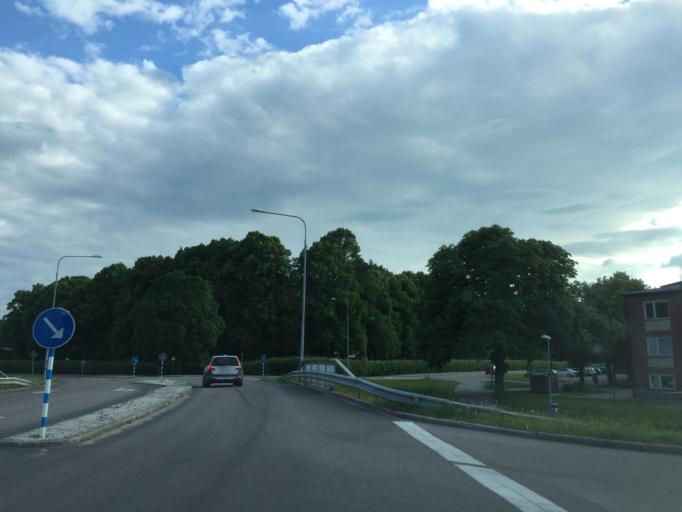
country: SE
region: Vaestmanland
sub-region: Arboga Kommun
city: Arboga
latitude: 59.3938
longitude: 15.8329
